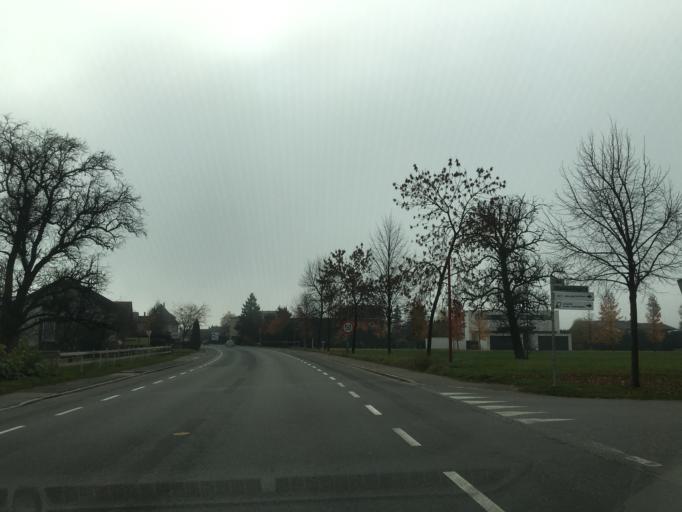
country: AT
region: Vorarlberg
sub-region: Politischer Bezirk Feldkirch
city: Gotzis
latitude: 47.3156
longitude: 9.6201
